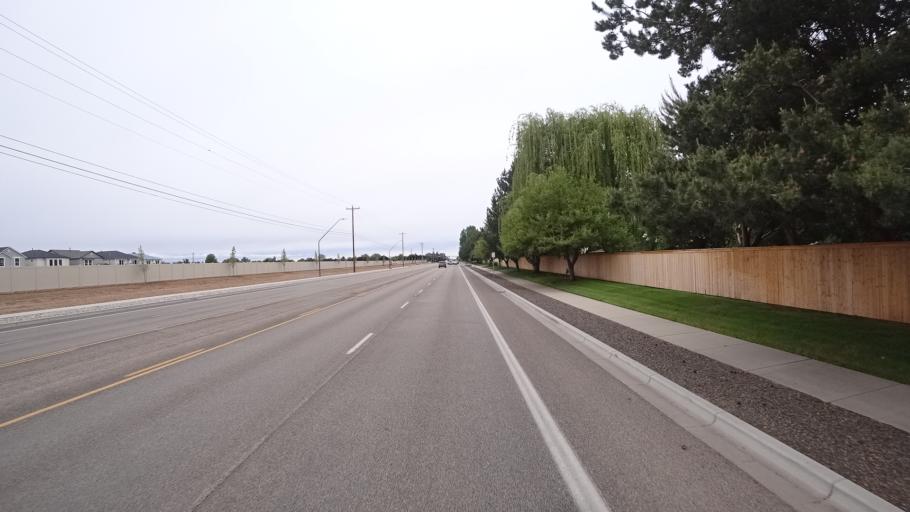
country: US
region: Idaho
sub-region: Ada County
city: Meridian
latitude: 43.6338
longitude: -116.3695
